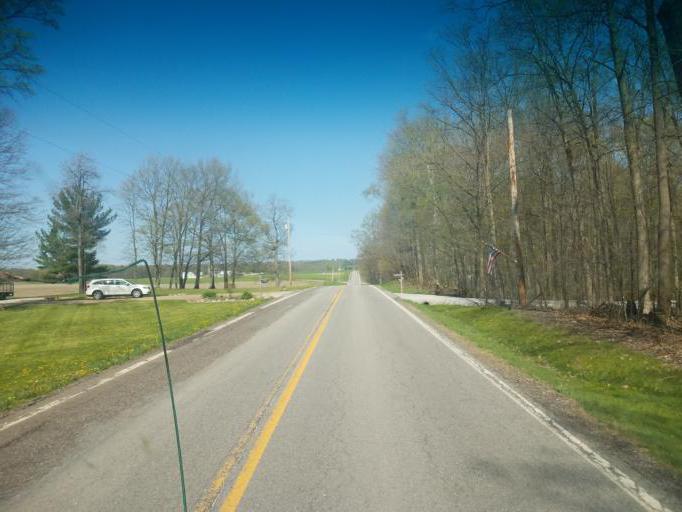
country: US
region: Ohio
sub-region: Wayne County
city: West Salem
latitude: 40.9297
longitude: -82.0367
